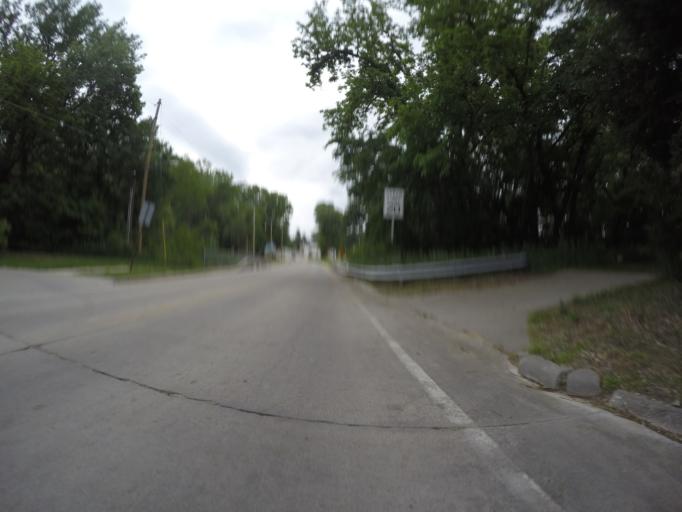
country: US
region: Kansas
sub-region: Pottawatomie County
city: Wamego
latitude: 39.1913
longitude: -96.4242
